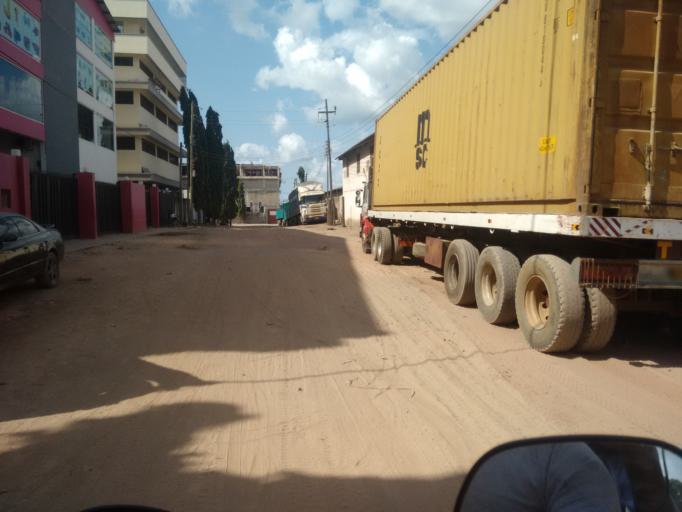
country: TZ
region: Dar es Salaam
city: Dar es Salaam
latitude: -6.8391
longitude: 39.2690
